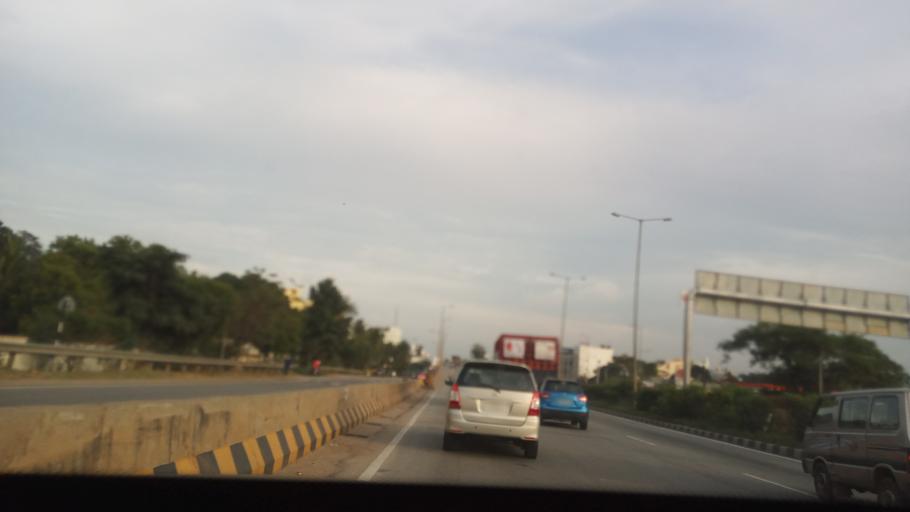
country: IN
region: Karnataka
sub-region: Bangalore Rural
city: Nelamangala
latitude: 13.0942
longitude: 77.3911
